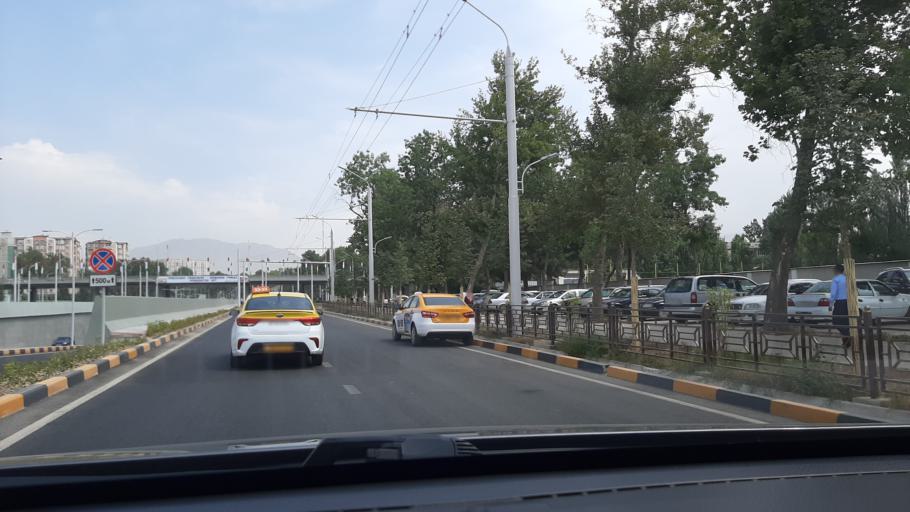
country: TJ
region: Dushanbe
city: Dushanbe
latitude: 38.5825
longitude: 68.7553
